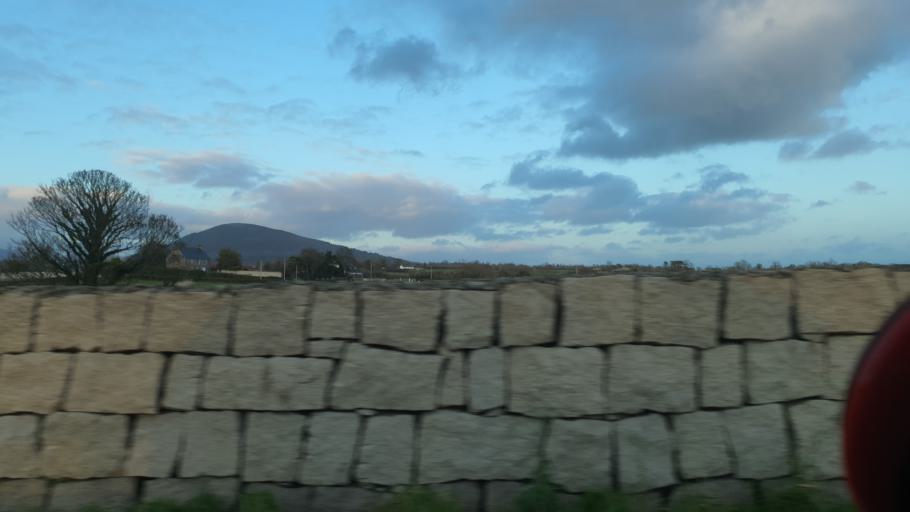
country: GB
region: Northern Ireland
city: Kilkeel
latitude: 54.0608
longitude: -6.0900
